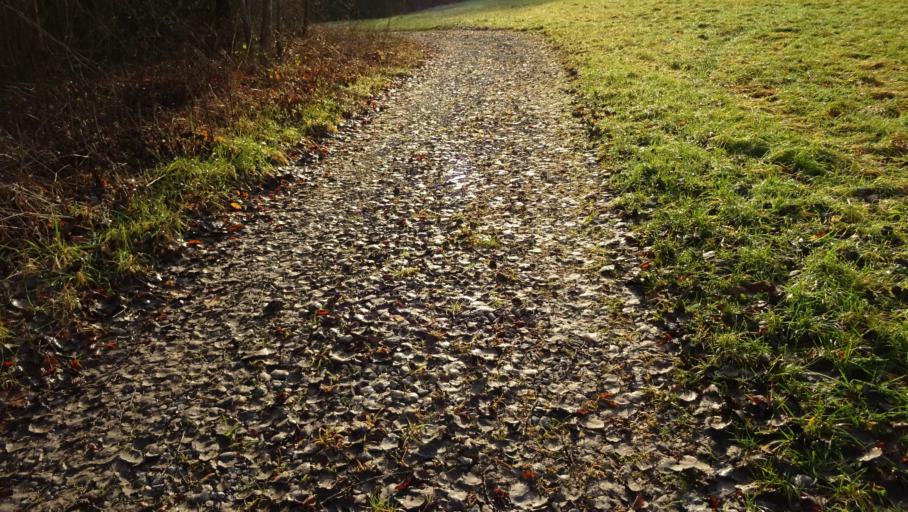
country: DE
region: Baden-Wuerttemberg
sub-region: Karlsruhe Region
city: Adelsheim
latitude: 49.4227
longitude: 9.4000
